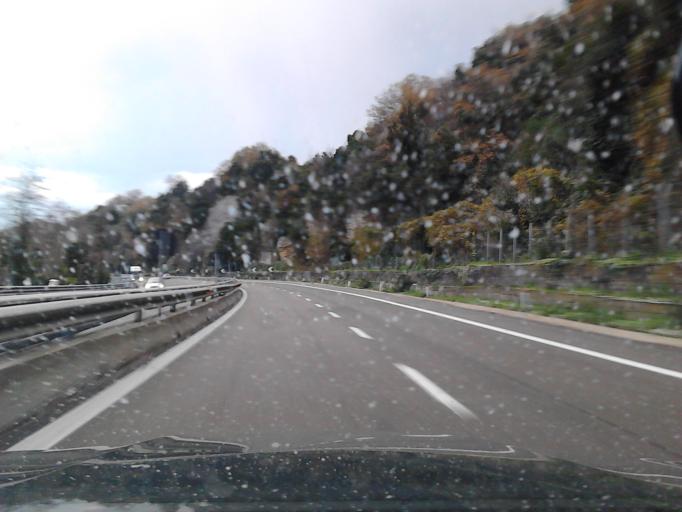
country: IT
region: Abruzzo
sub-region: Provincia di Chieti
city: Treglio
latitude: 42.2731
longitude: 14.4351
